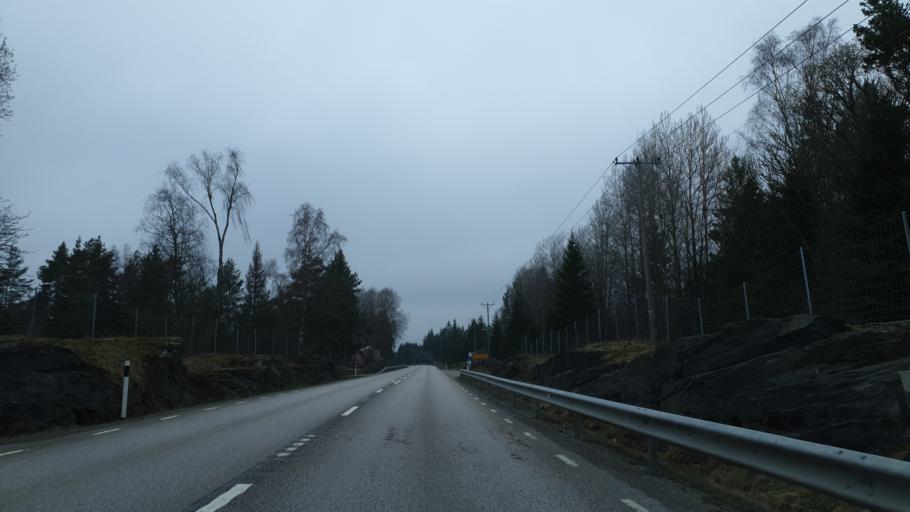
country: SE
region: Vaestra Goetaland
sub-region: Harryda Kommun
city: Hindas
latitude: 57.6344
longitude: 12.4097
